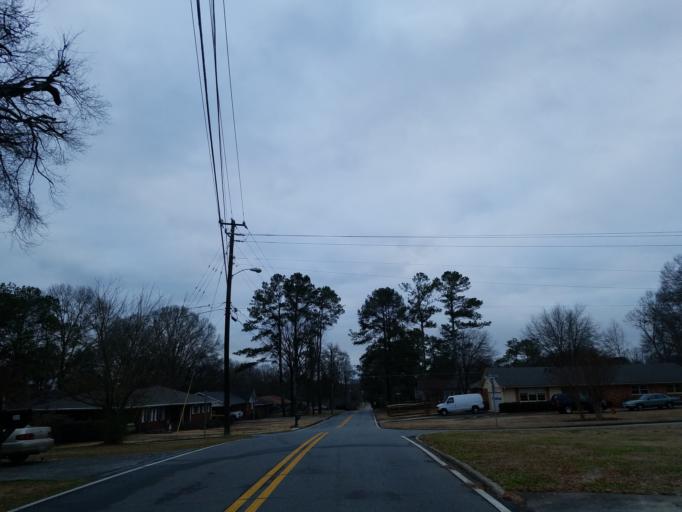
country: US
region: Georgia
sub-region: Bartow County
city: Cartersville
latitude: 34.1581
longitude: -84.7989
